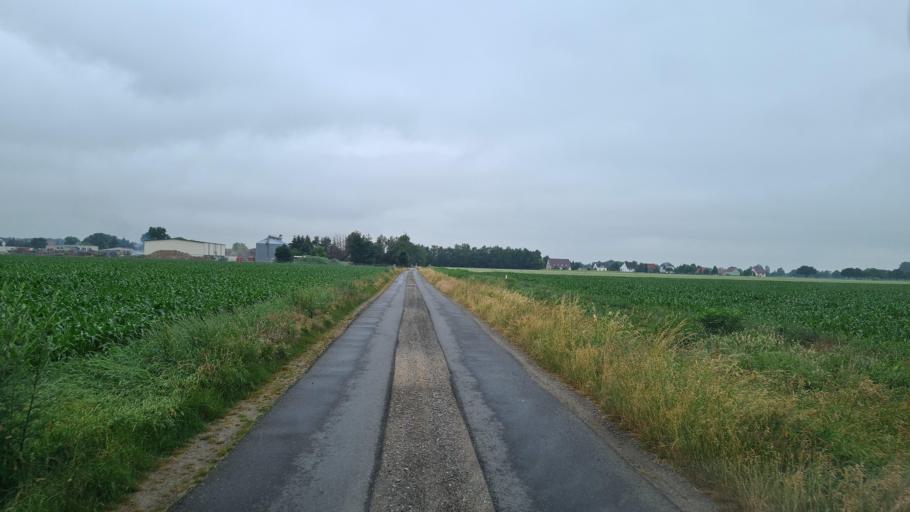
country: DE
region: Brandenburg
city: Grosskmehlen
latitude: 51.3894
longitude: 13.7186
